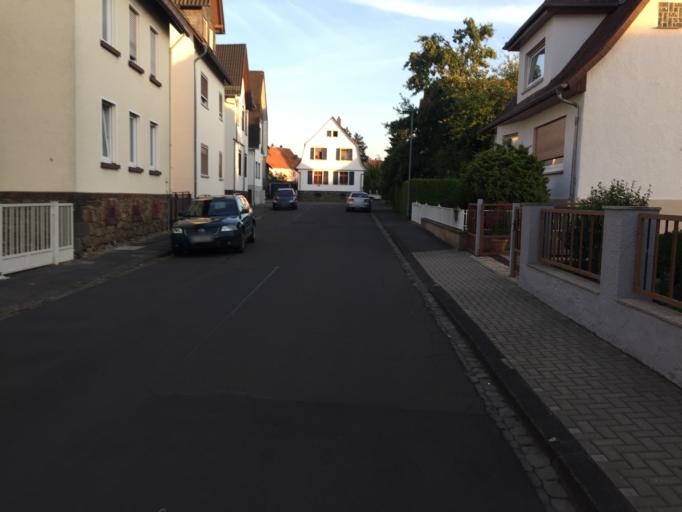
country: DE
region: Hesse
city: Allendorf an der Lahn
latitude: 50.5574
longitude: 8.6469
